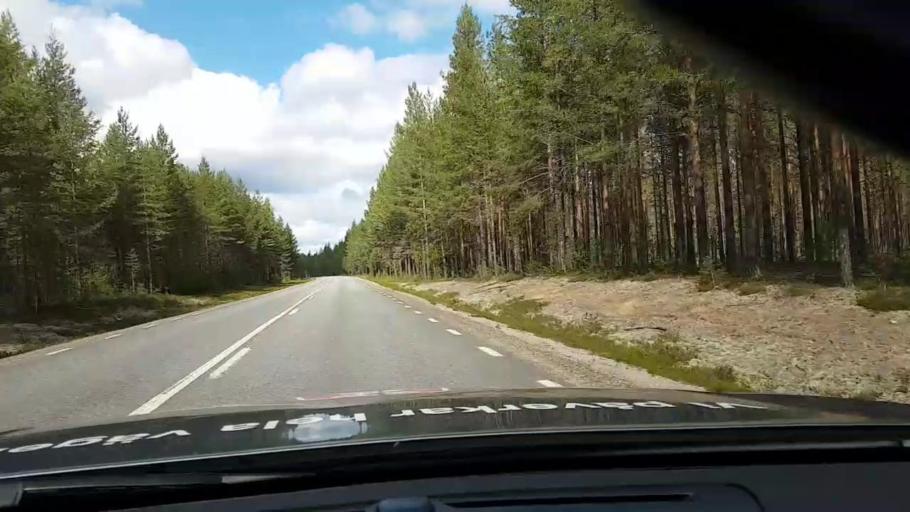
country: SE
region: Vaesternorrland
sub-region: OErnskoeldsviks Kommun
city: Bredbyn
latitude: 63.5337
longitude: 17.9666
